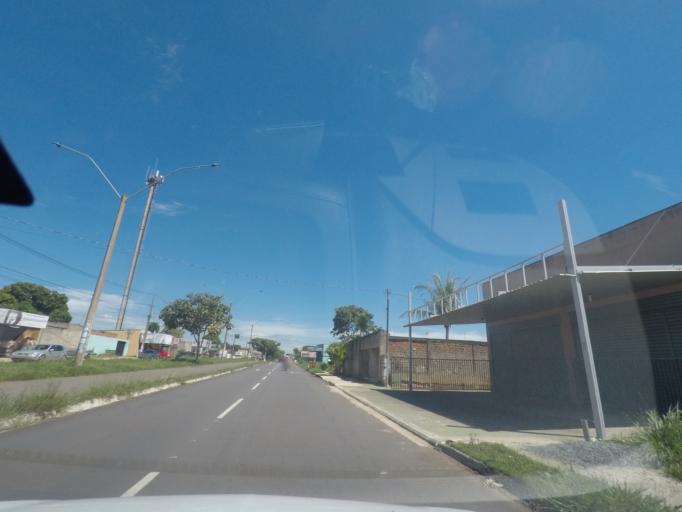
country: BR
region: Goias
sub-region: Aparecida De Goiania
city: Aparecida de Goiania
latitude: -16.7745
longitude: -49.3382
